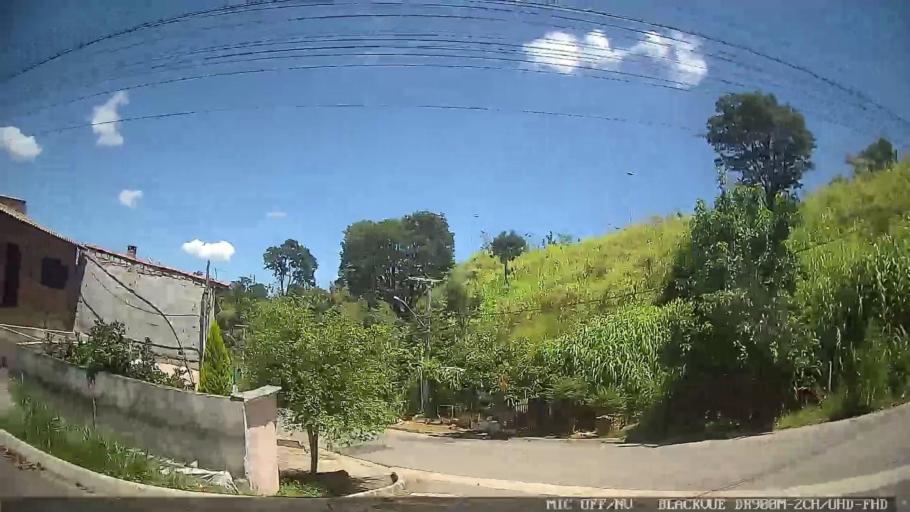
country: BR
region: Sao Paulo
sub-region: Atibaia
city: Atibaia
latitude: -23.1007
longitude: -46.5649
